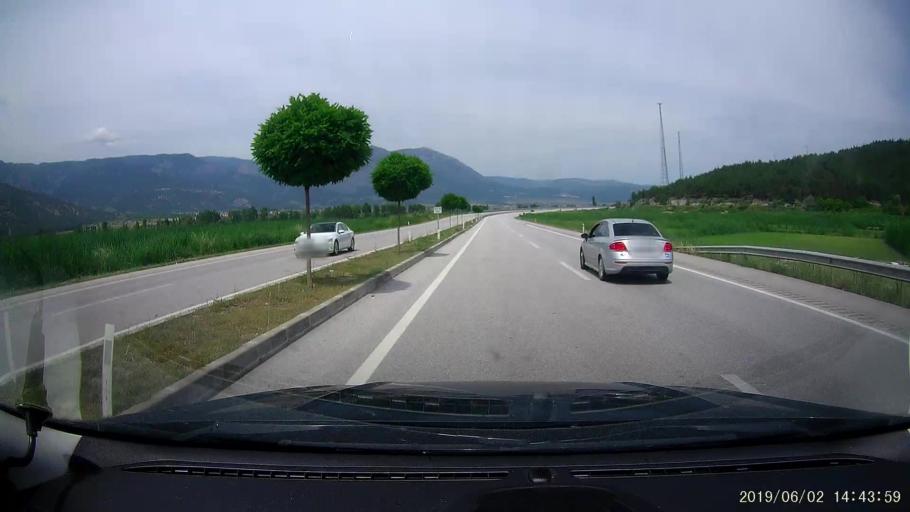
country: TR
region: Corum
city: Hacihamza
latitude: 41.0996
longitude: 34.4024
